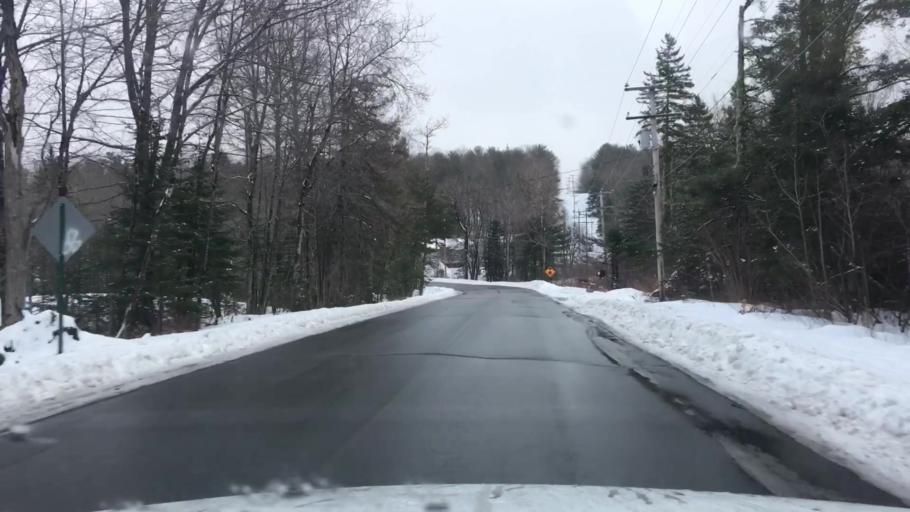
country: US
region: Maine
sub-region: Hancock County
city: Trenton
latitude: 44.4063
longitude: -68.3211
